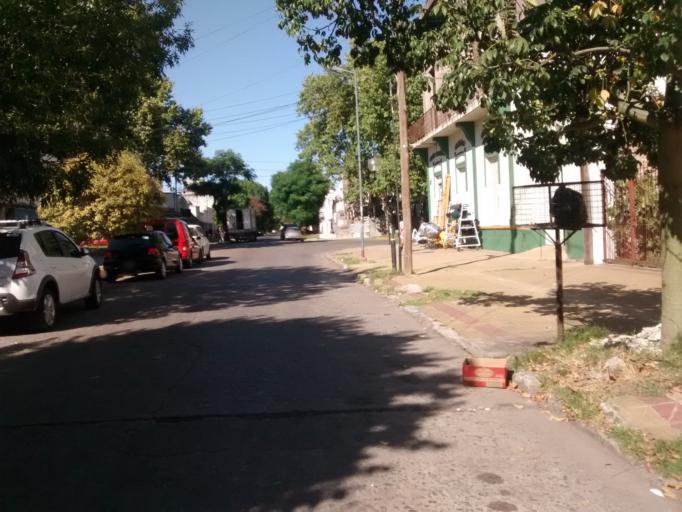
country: AR
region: Buenos Aires
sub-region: Partido de La Plata
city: La Plata
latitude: -34.9217
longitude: -57.9259
